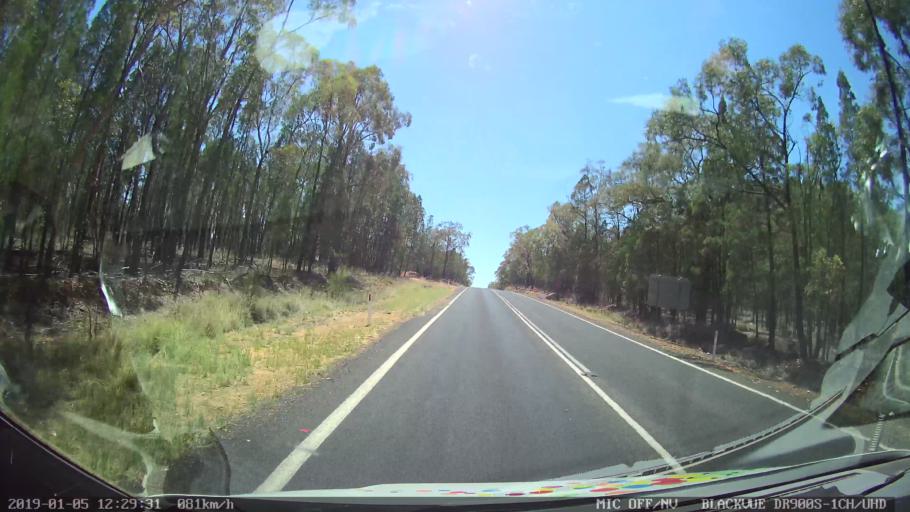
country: AU
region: New South Wales
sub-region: Warrumbungle Shire
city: Coonabarabran
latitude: -31.2327
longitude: 149.3381
